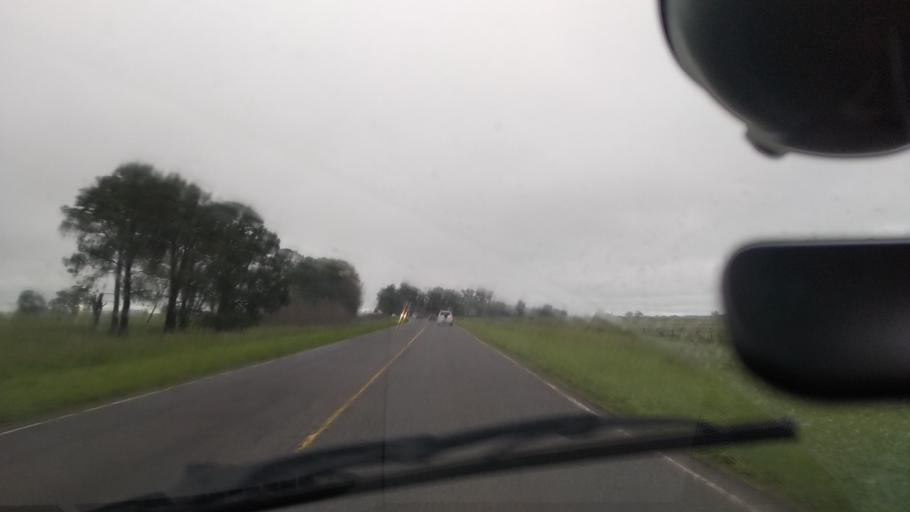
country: AR
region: Buenos Aires
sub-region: Partido de Magdalena
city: Magdalena
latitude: -35.2133
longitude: -57.7506
